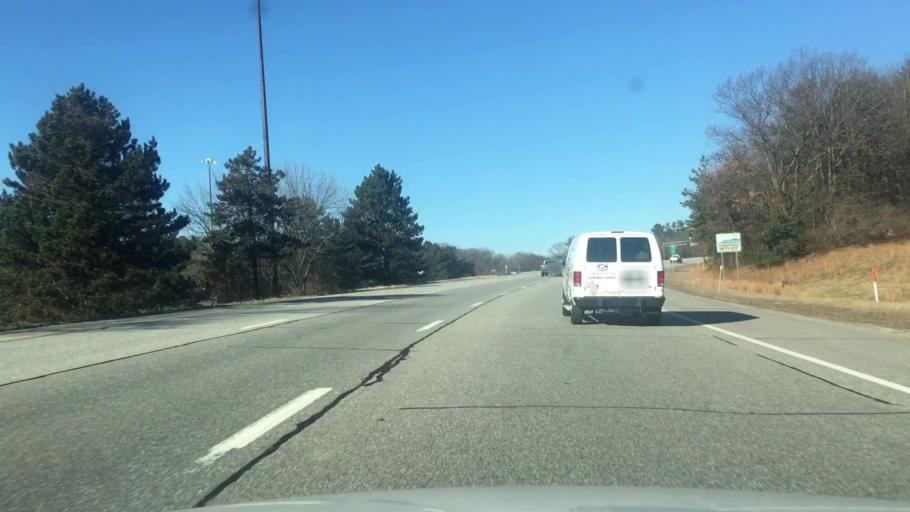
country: US
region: New Hampshire
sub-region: Hillsborough County
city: Manchester
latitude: 43.0002
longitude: -71.4303
